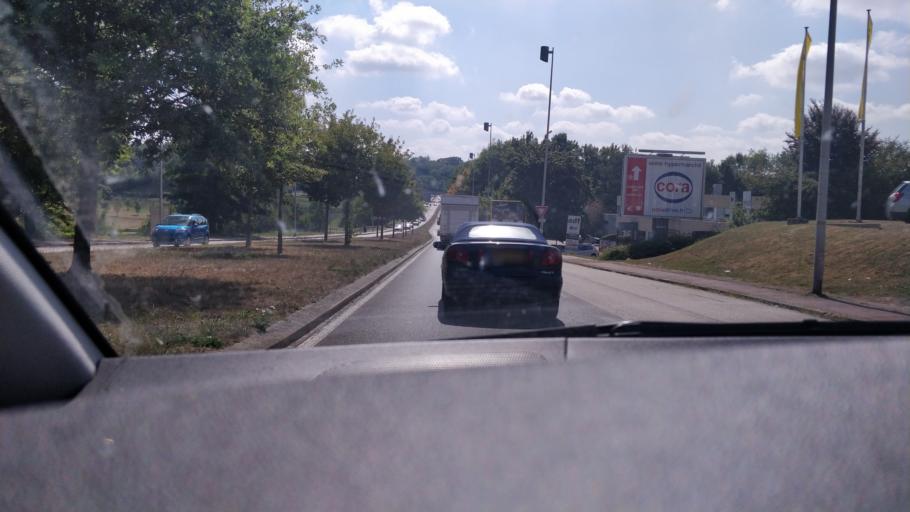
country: FR
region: Limousin
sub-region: Departement de la Haute-Vienne
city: Couzeix
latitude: 45.8666
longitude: 1.2699
